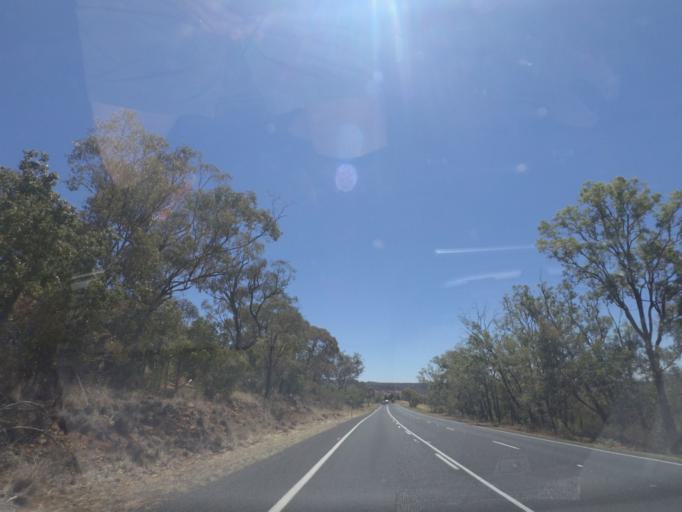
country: AU
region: New South Wales
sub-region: Warrumbungle Shire
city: Coonabarabran
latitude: -31.4541
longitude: 149.0019
